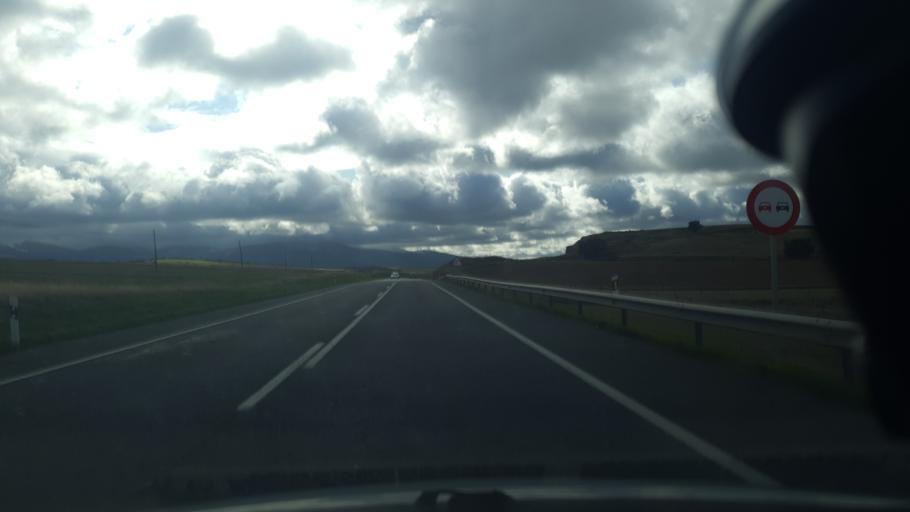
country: ES
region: Castille and Leon
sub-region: Provincia de Segovia
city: Segovia
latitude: 40.9124
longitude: -4.1589
